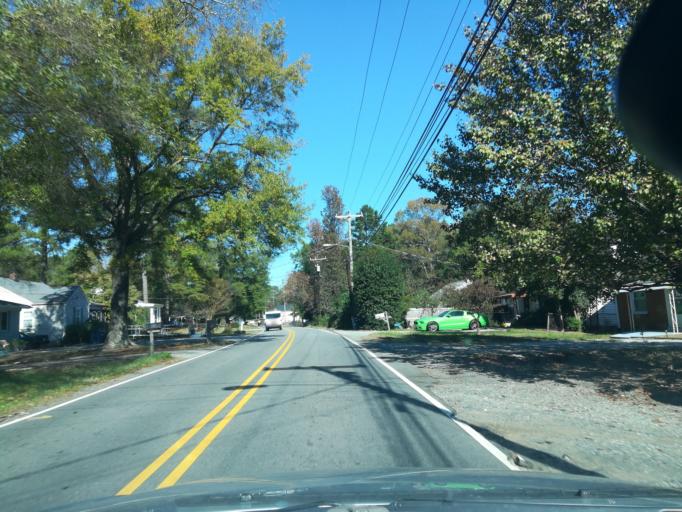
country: US
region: North Carolina
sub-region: Durham County
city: Durham
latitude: 36.0382
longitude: -78.9081
